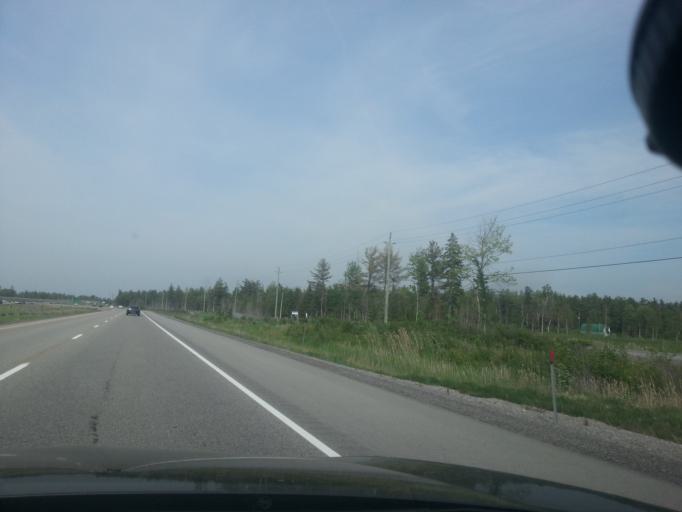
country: CA
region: Ontario
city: Bells Corners
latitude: 45.2416
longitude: -75.9768
